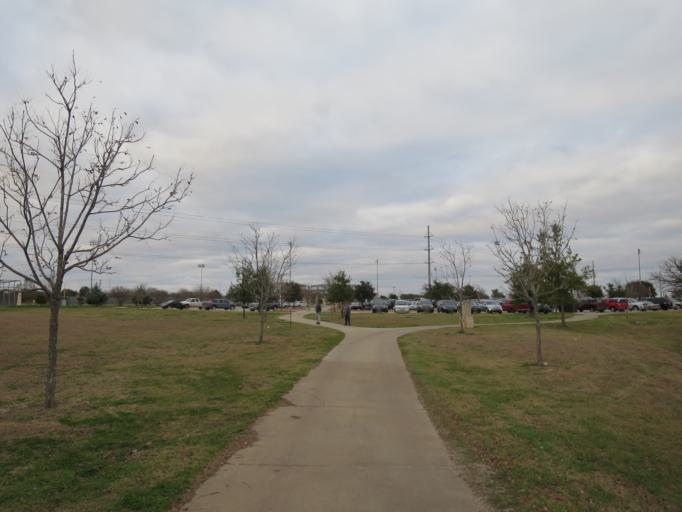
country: US
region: Texas
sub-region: Williamson County
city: Round Rock
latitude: 30.5441
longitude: -97.6202
